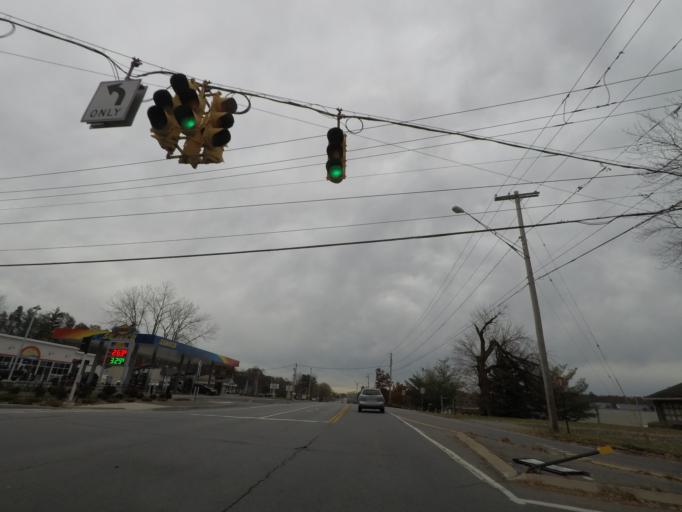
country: US
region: New York
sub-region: Schenectady County
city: Niskayuna
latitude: 42.8189
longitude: -73.7756
